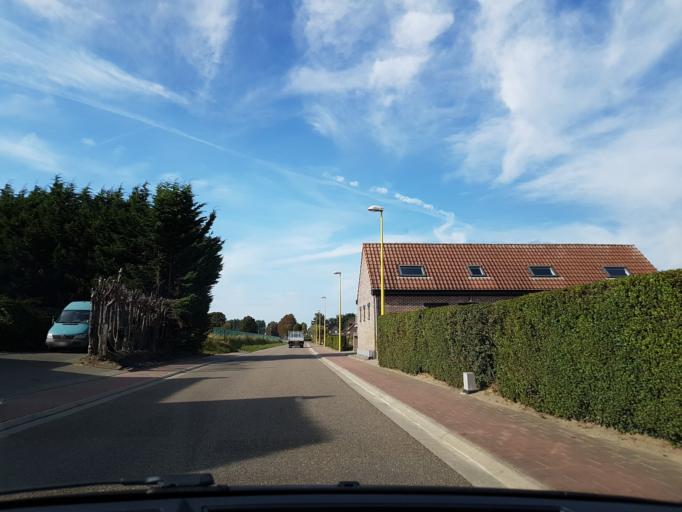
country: BE
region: Flanders
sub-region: Provincie Vlaams-Brabant
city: Grimbergen
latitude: 50.9520
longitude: 4.3949
